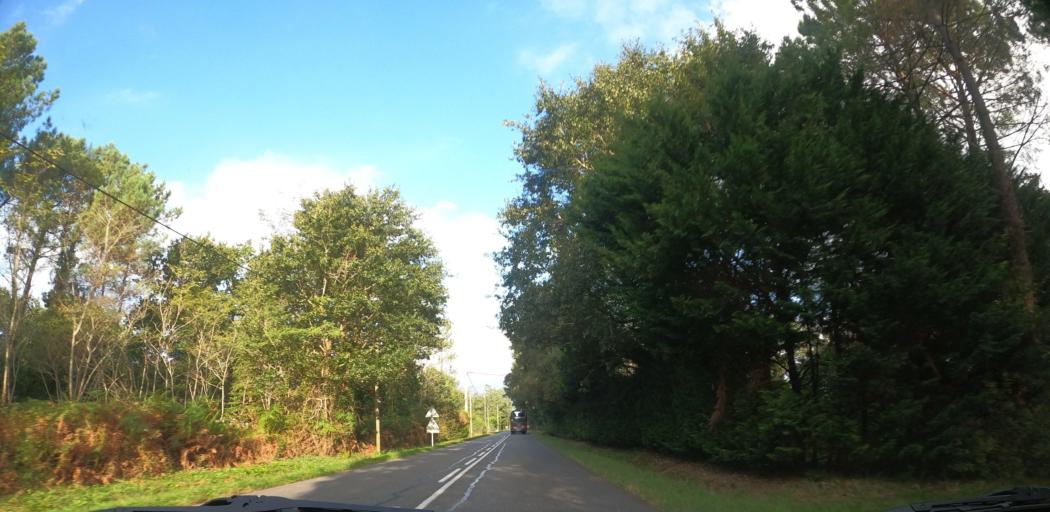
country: FR
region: Aquitaine
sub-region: Departement des Landes
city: Soustons
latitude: 43.7292
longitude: -1.2842
